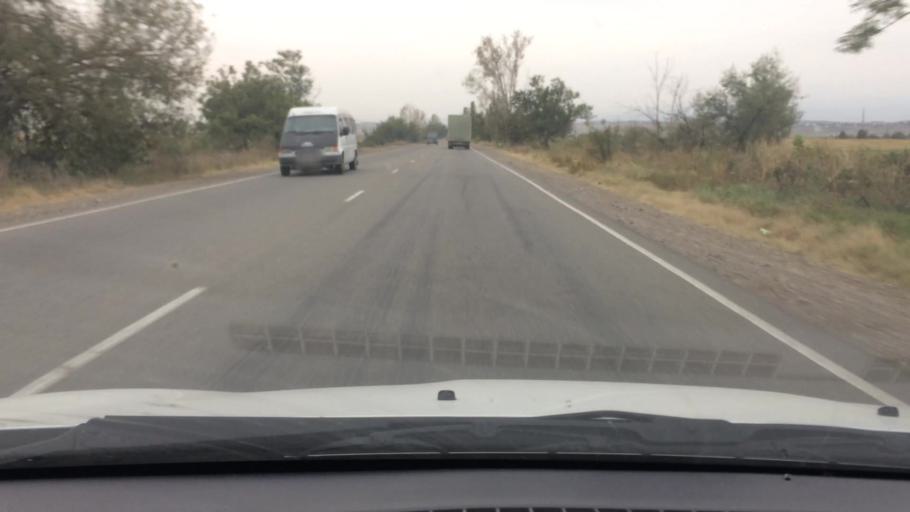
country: GE
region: Kvemo Kartli
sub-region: Marneuli
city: Marneuli
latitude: 41.5592
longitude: 44.7758
